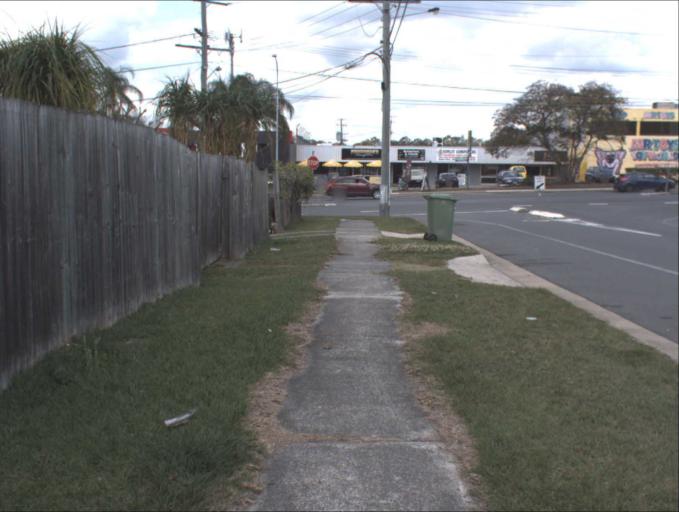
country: AU
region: Queensland
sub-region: Brisbane
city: Sunnybank Hills
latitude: -27.6619
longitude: 153.0506
